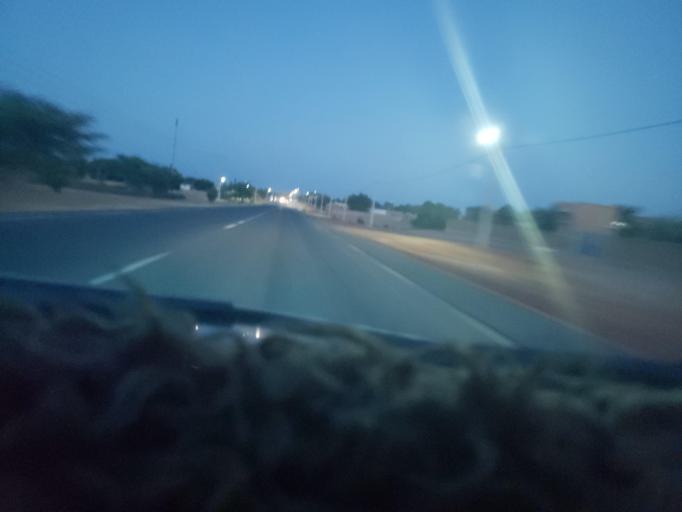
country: SN
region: Louga
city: Ndibene Dahra
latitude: 15.3820
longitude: -15.2432
